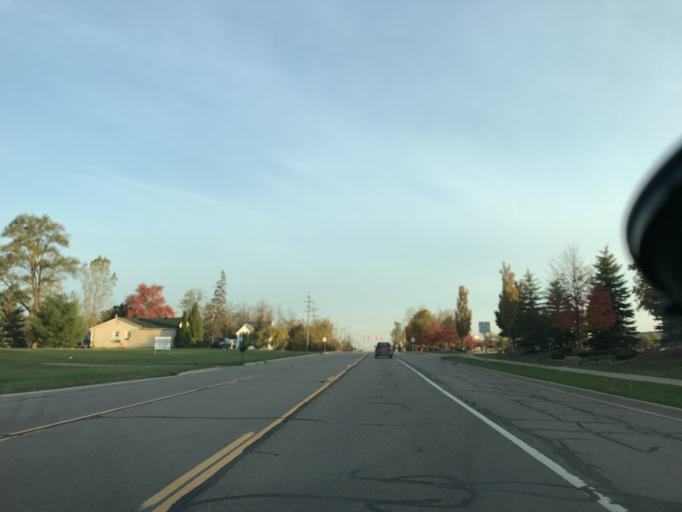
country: US
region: Michigan
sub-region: Oakland County
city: Wixom
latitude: 42.4873
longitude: -83.5353
